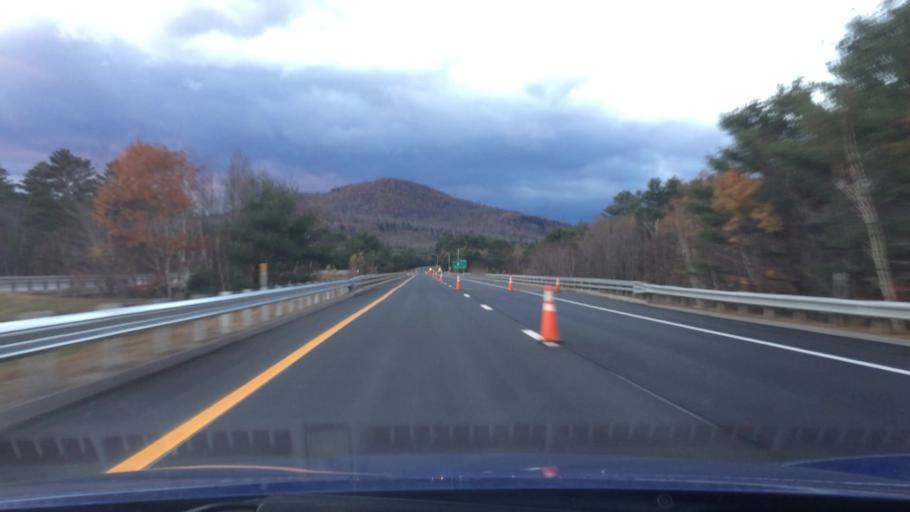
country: US
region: New Hampshire
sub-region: Grafton County
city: Thornton
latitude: 43.8671
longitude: -71.6633
